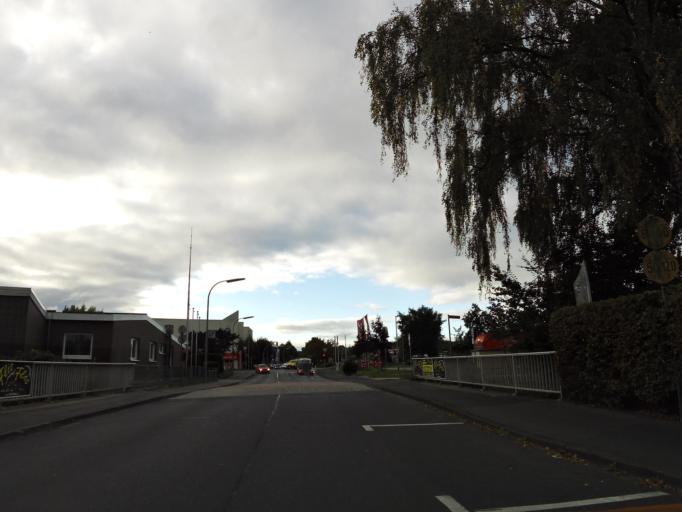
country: DE
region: Lower Saxony
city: Rosdorf
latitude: 51.5294
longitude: 9.8902
